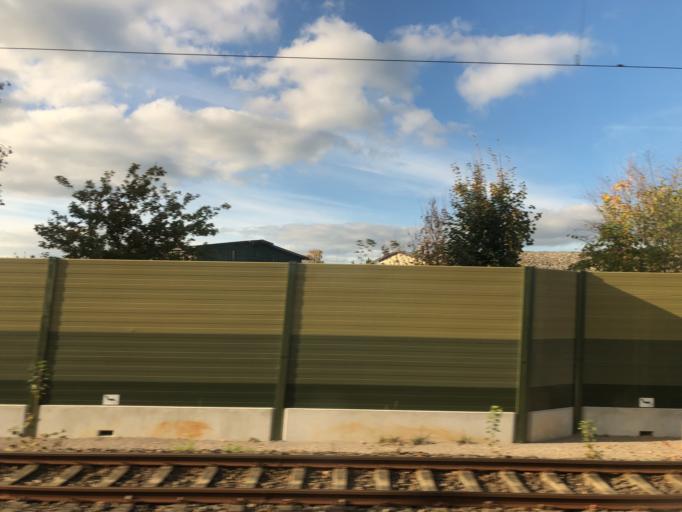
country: DE
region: Schleswig-Holstein
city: Brokstedt
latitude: 53.9885
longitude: 9.8210
